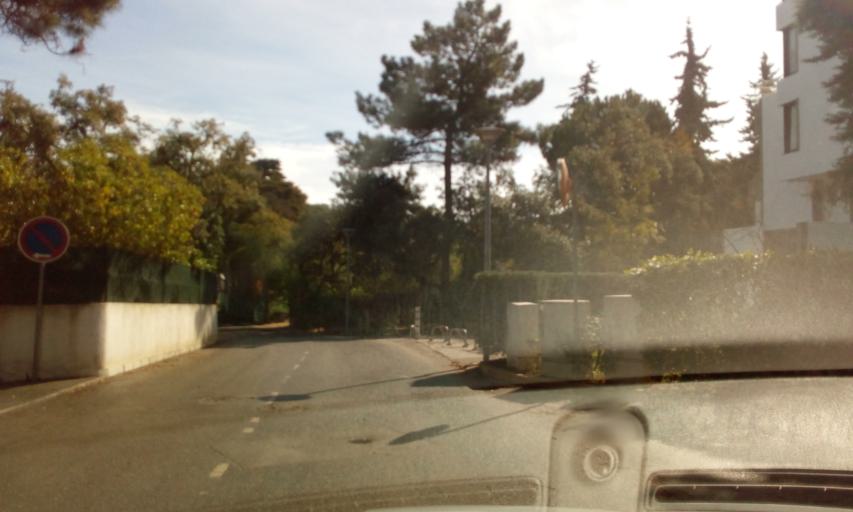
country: PT
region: Faro
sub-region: Albufeira
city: Albufeira
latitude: 37.0922
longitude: -8.2044
